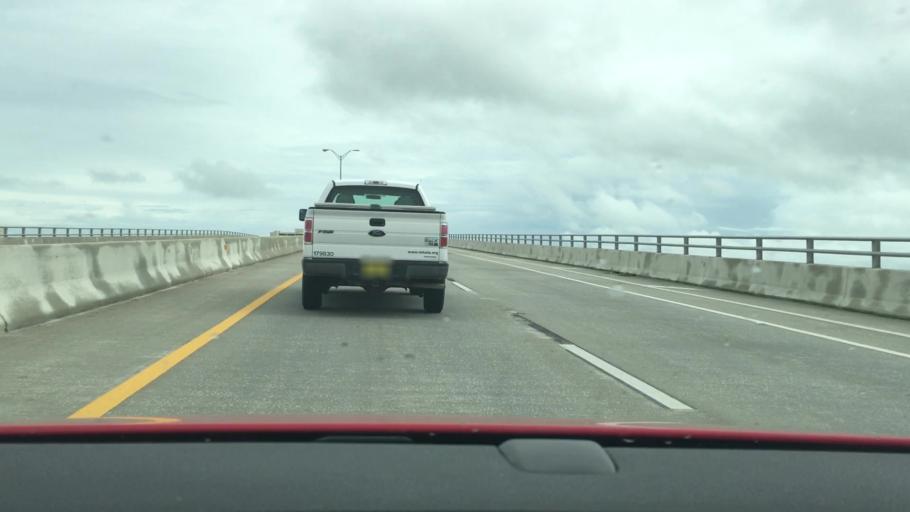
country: US
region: Florida
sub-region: Volusia County
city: Port Orange
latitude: 29.1475
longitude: -80.9771
